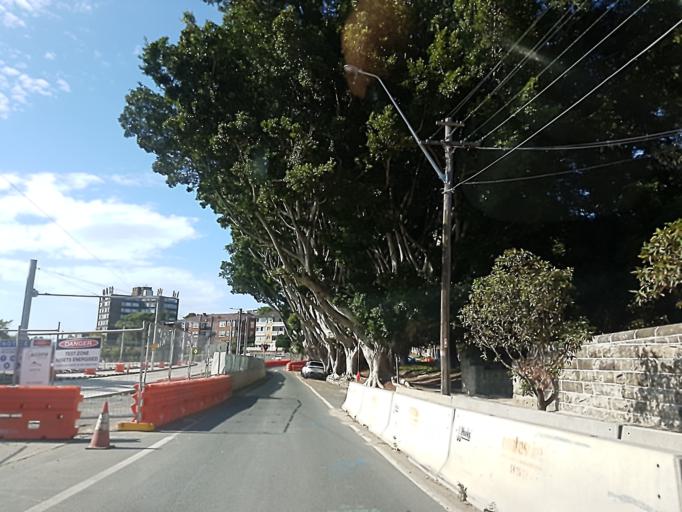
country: AU
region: New South Wales
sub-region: Randwick
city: Randwick
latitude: -33.9122
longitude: 151.2356
